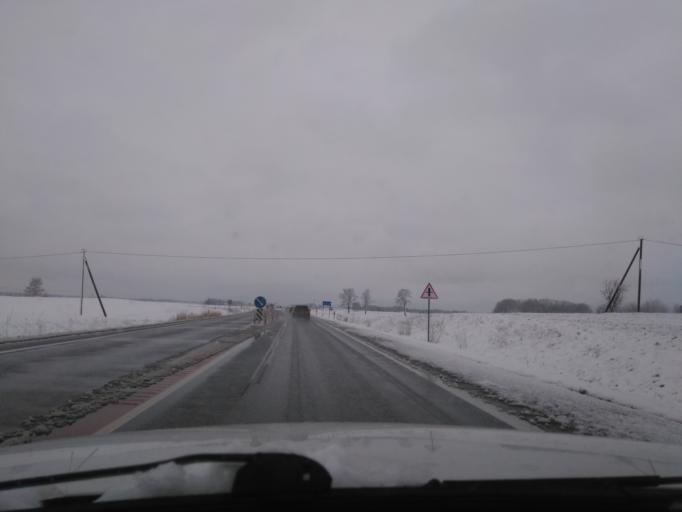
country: LT
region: Kauno apskritis
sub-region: Kauno rajonas
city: Mastaiciai
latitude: 54.7515
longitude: 23.7292
